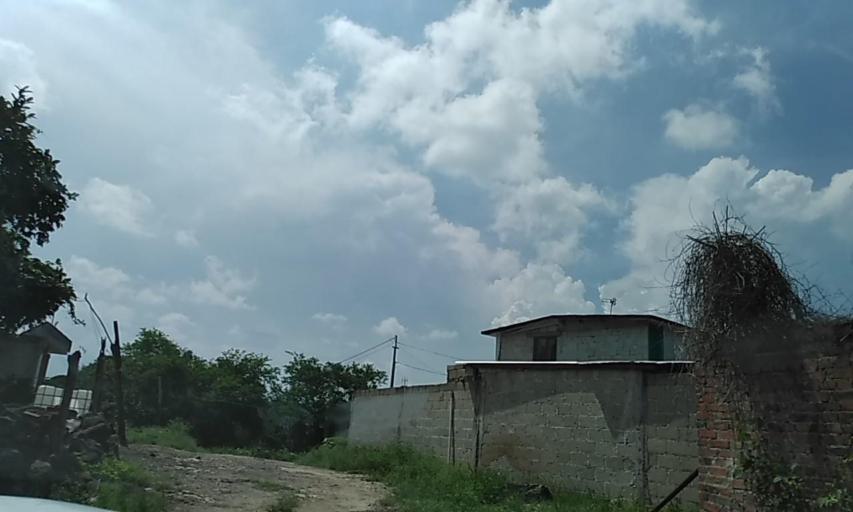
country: MX
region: Veracruz
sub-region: Emiliano Zapata
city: Dos Rios
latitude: 19.4420
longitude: -96.7827
